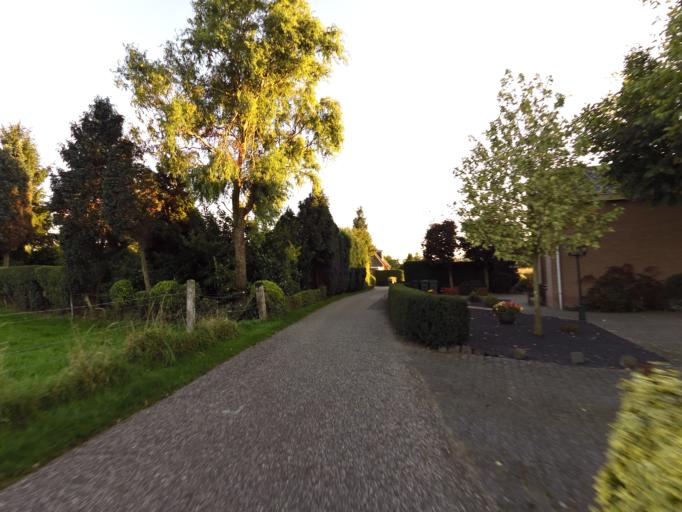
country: NL
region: Gelderland
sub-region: Gemeente Doesburg
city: Doesburg
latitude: 51.9362
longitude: 6.1504
